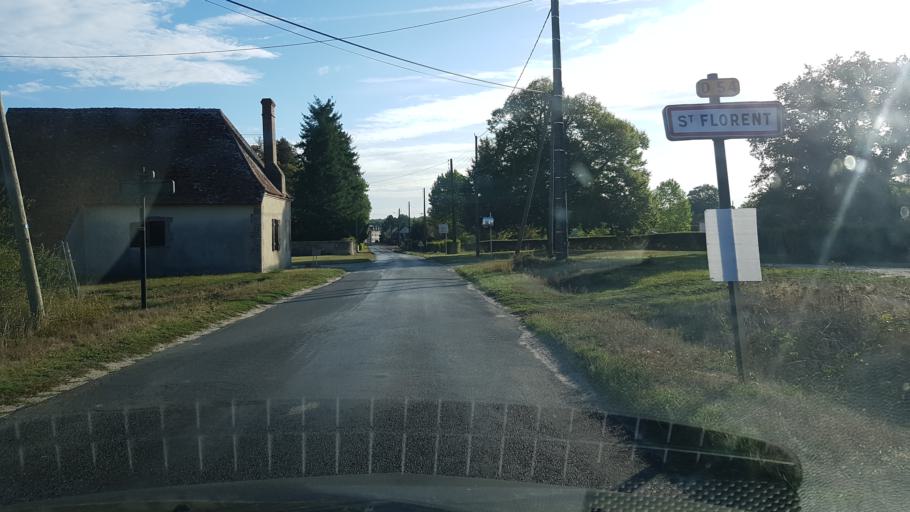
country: FR
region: Centre
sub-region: Departement du Loiret
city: Coullons
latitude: 47.6882
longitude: 2.4687
